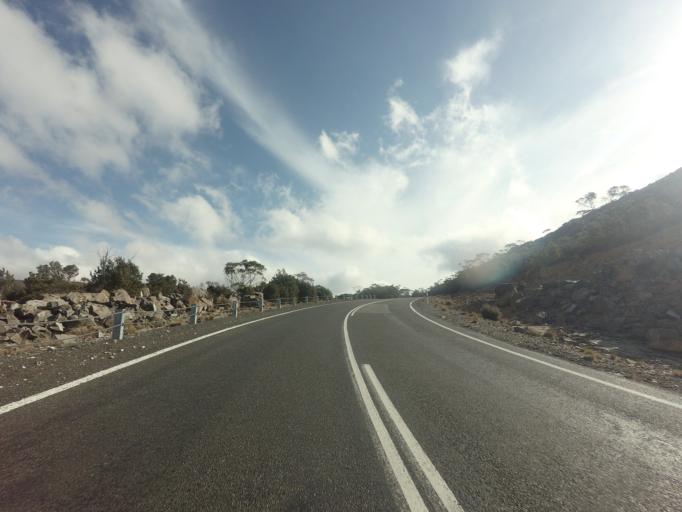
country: AU
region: Tasmania
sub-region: Meander Valley
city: Deloraine
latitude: -41.7308
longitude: 146.7167
